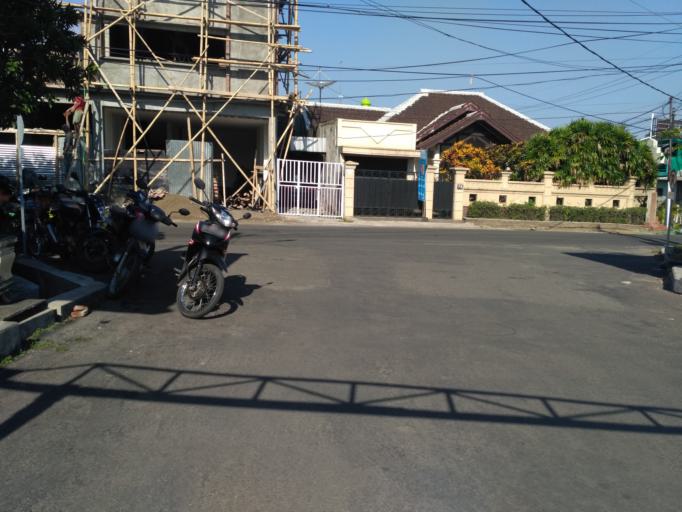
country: ID
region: East Java
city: Malang
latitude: -7.9427
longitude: 112.6289
